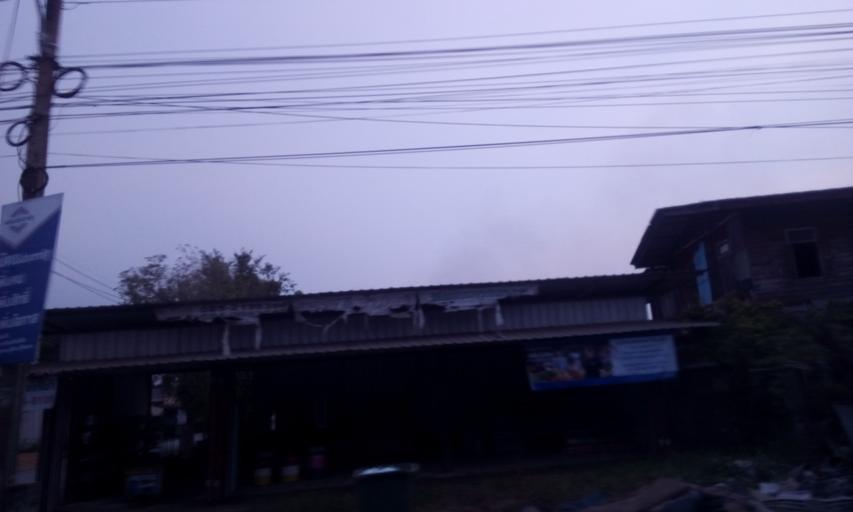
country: TH
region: Bangkok
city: Nong Chok
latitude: 13.8447
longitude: 100.8969
